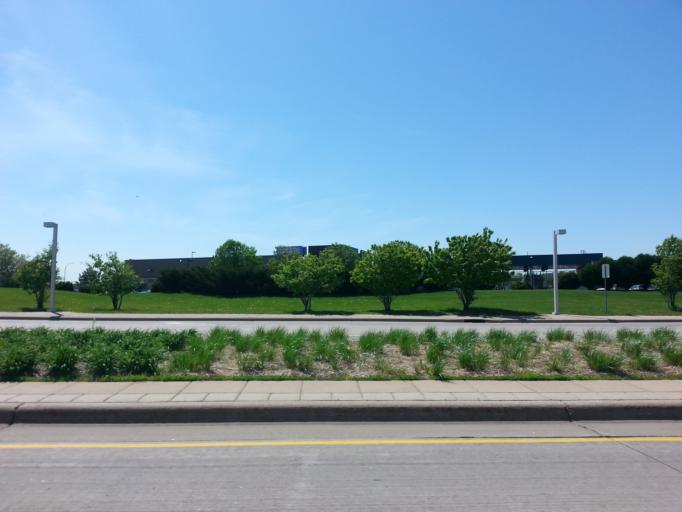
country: US
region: Minnesota
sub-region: Hennepin County
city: Richfield
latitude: 44.8636
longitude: -93.2376
